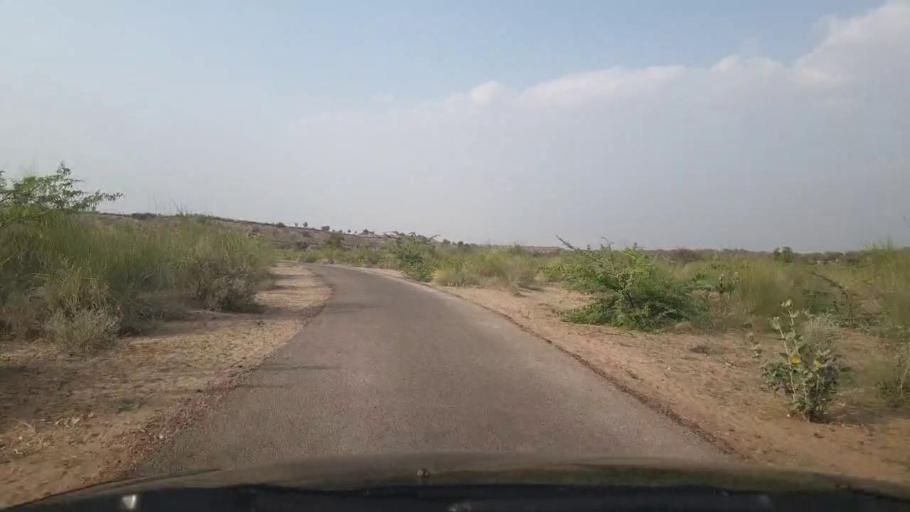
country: PK
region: Sindh
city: Islamkot
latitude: 25.0712
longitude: 70.5658
